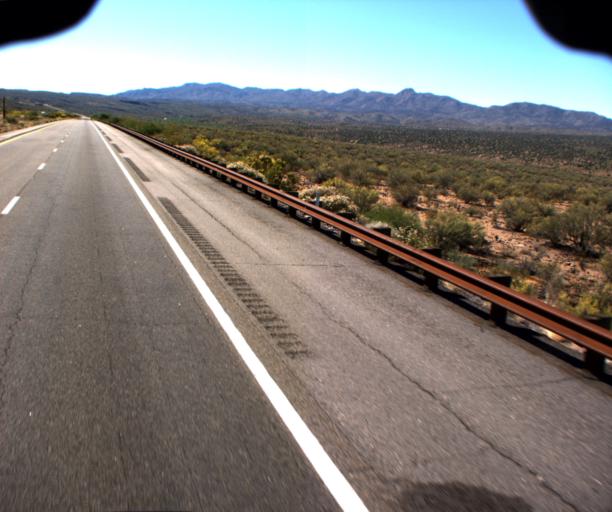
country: US
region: Arizona
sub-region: Yavapai County
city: Bagdad
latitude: 34.5266
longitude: -113.4278
